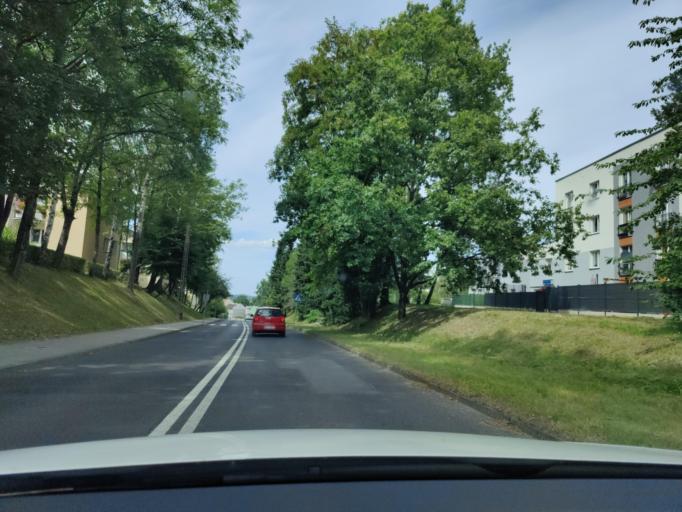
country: PL
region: Opole Voivodeship
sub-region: Powiat nyski
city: Glucholazy
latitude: 50.3087
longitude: 17.3912
